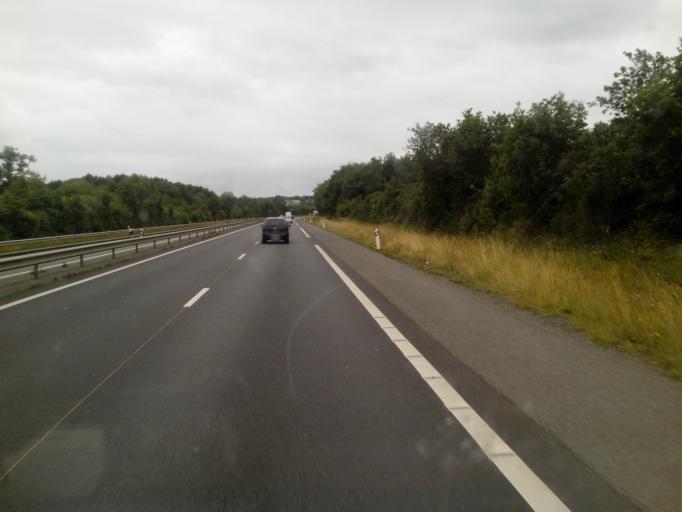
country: FR
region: Brittany
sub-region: Departement d'Ille-et-Vilaine
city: Orgeres
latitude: 48.0008
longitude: -1.6933
